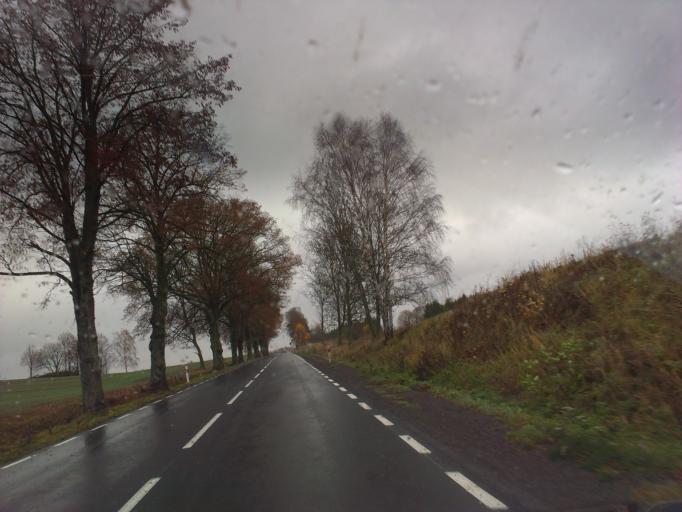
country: PL
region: West Pomeranian Voivodeship
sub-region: Powiat szczecinecki
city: Lubowo
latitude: 53.5902
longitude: 16.4031
